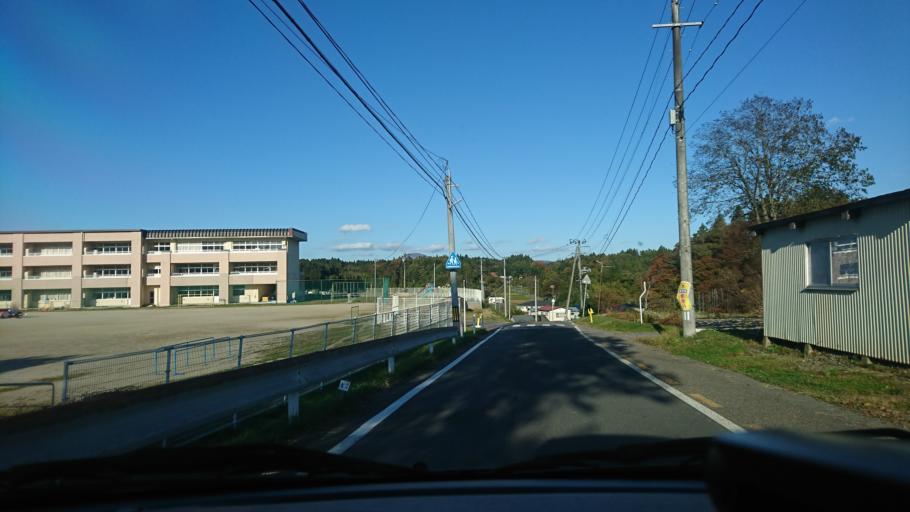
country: JP
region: Iwate
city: Ichinoseki
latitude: 38.8654
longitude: 141.3521
